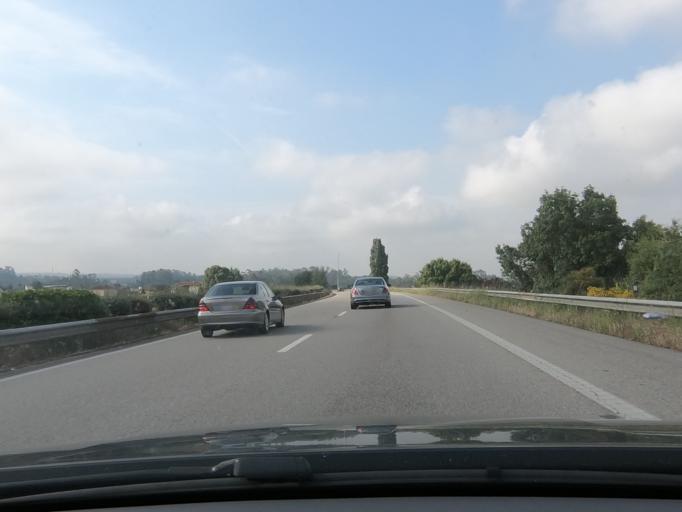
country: PT
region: Aveiro
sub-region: Estarreja
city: Beduido
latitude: 40.7700
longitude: -8.5438
